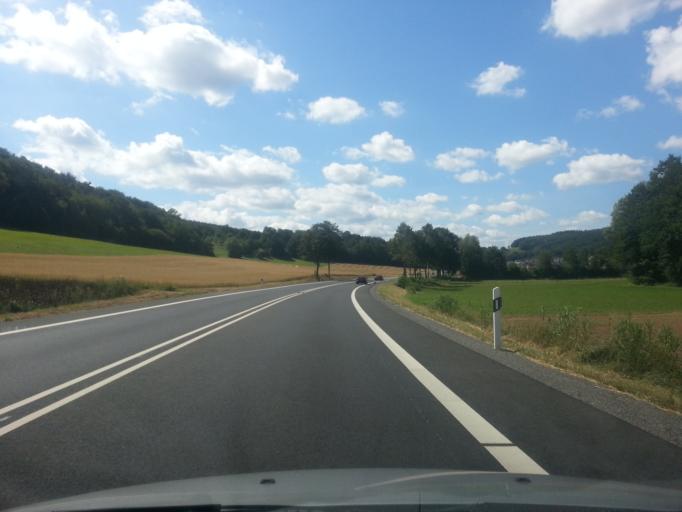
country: DE
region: Hesse
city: Hochst im Odenwald
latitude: 49.7804
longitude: 8.9947
